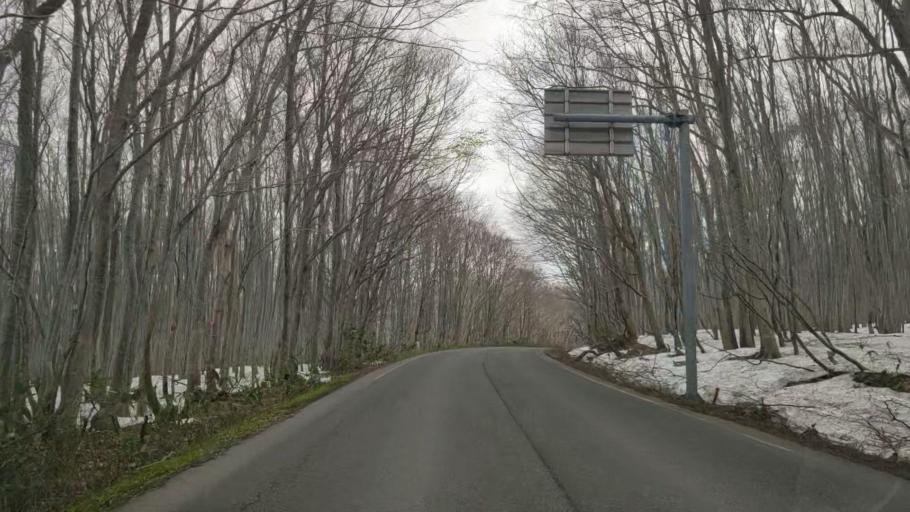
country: JP
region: Aomori
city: Aomori Shi
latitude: 40.6966
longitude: 140.9057
